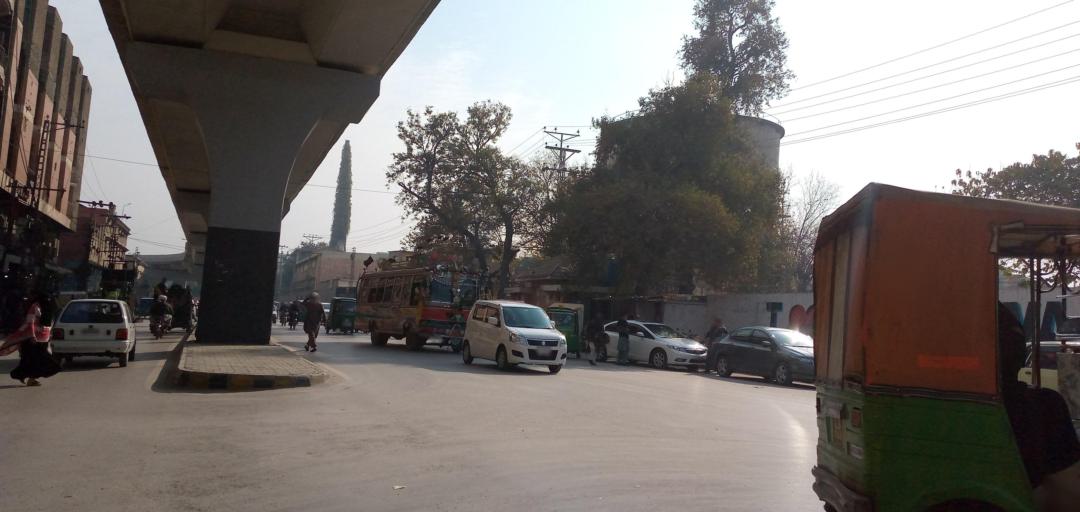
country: PK
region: Khyber Pakhtunkhwa
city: Peshawar
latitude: 33.9957
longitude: 71.5360
